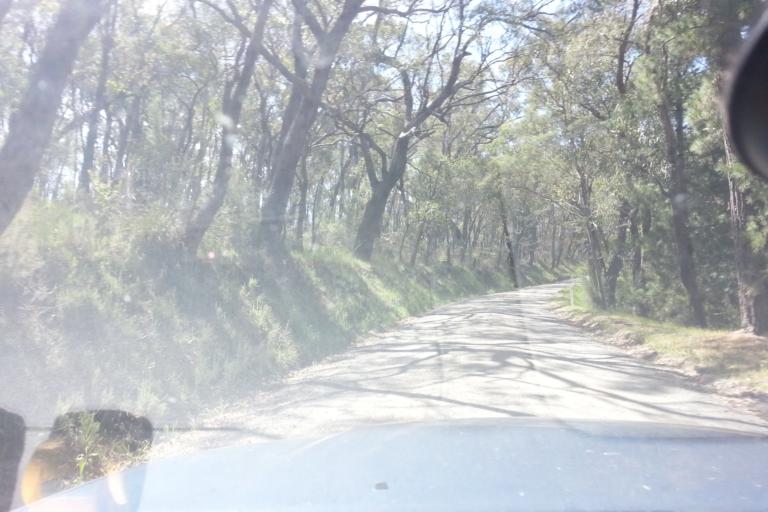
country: AU
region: Victoria
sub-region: Cardinia
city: Pakenham Upper
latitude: -37.9985
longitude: 145.4858
